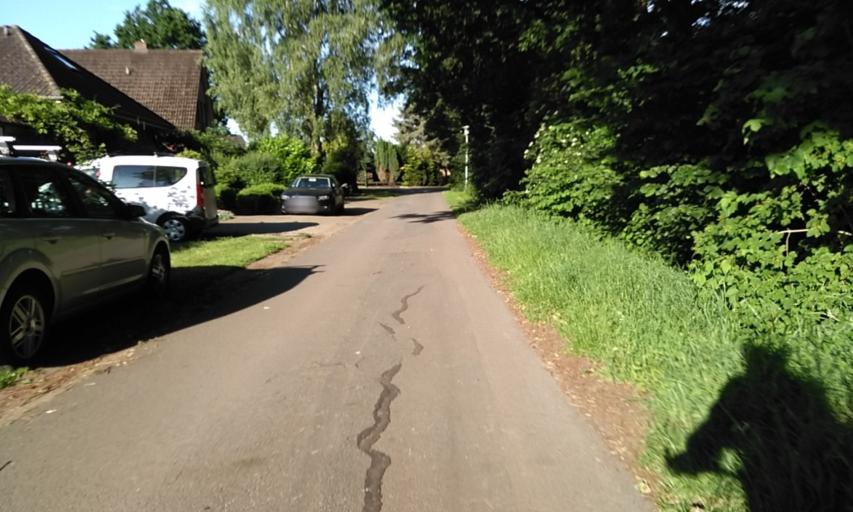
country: DE
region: Lower Saxony
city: Deinste
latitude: 53.5284
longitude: 9.4503
